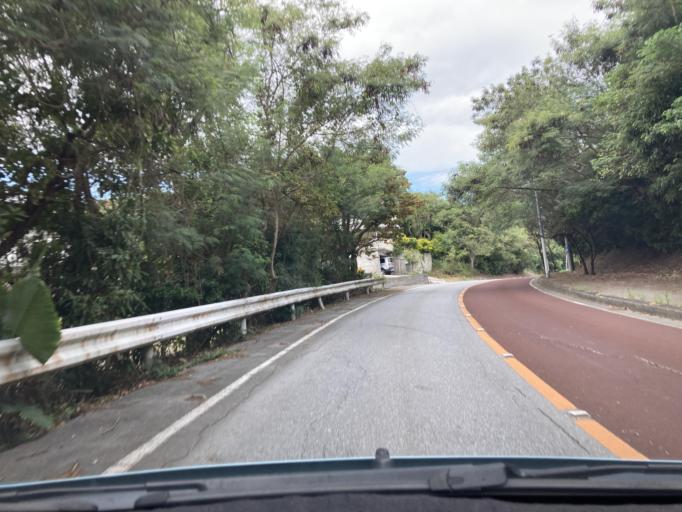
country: JP
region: Okinawa
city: Ginowan
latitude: 26.2576
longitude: 127.7839
